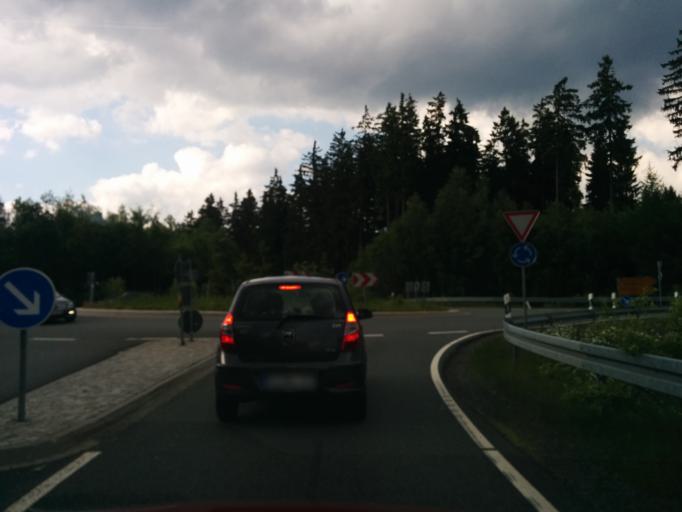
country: DE
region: Lower Saxony
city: Braunlage
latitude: 51.7135
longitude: 10.6229
